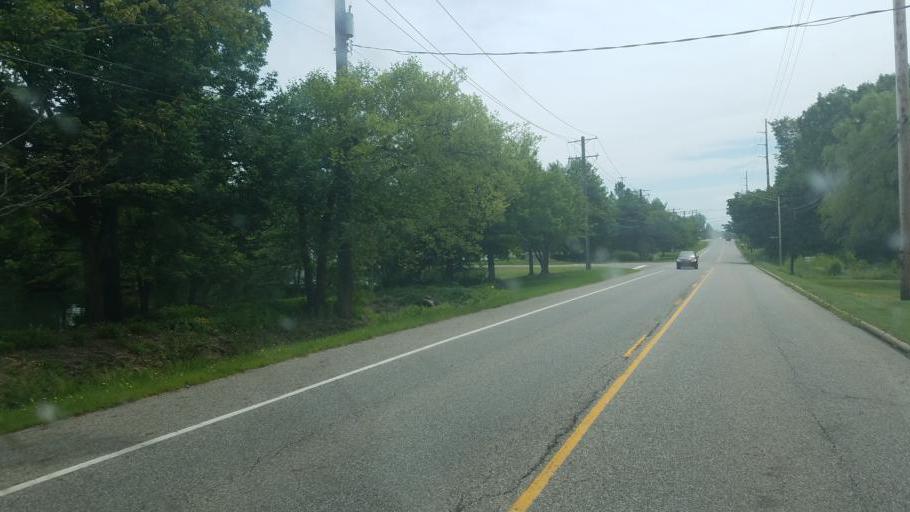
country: US
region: Ohio
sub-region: Geauga County
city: Bainbridge
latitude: 41.3951
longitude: -81.2959
